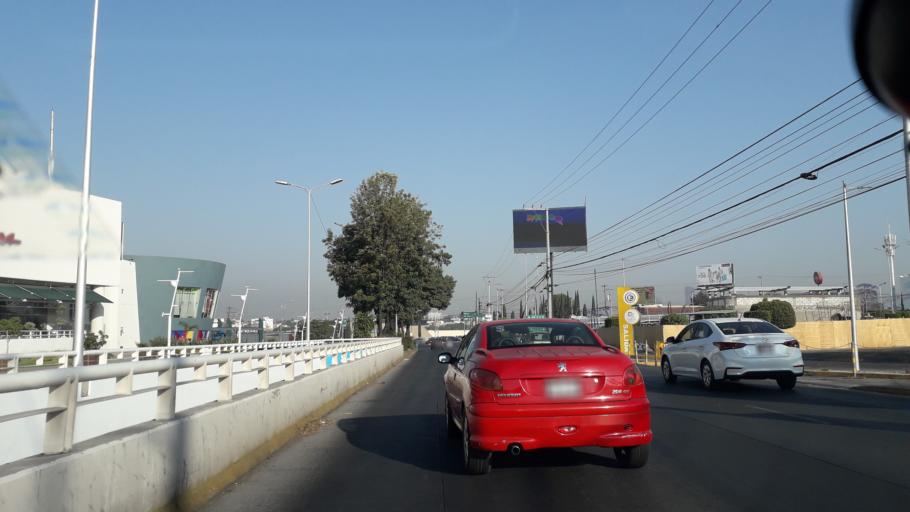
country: MX
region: Puebla
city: Puebla
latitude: 19.0438
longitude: -98.2342
